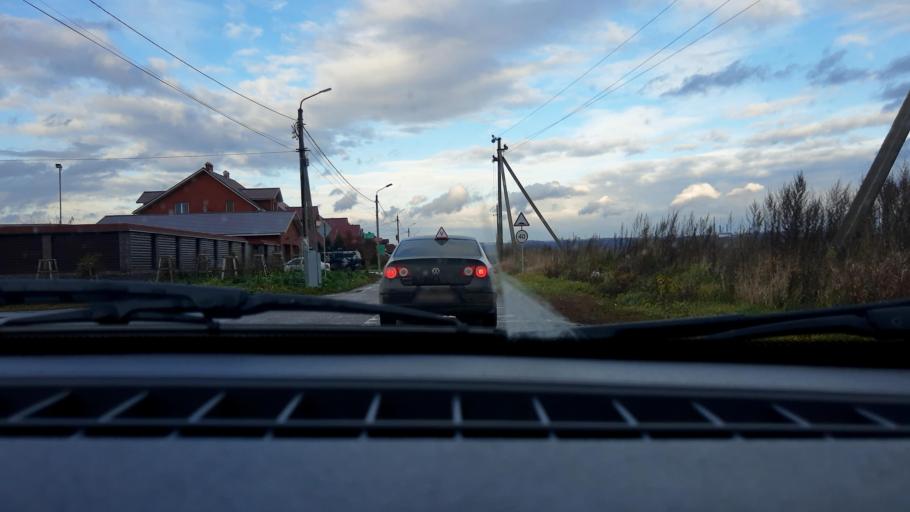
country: RU
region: Bashkortostan
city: Ufa
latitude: 54.8542
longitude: 56.0172
